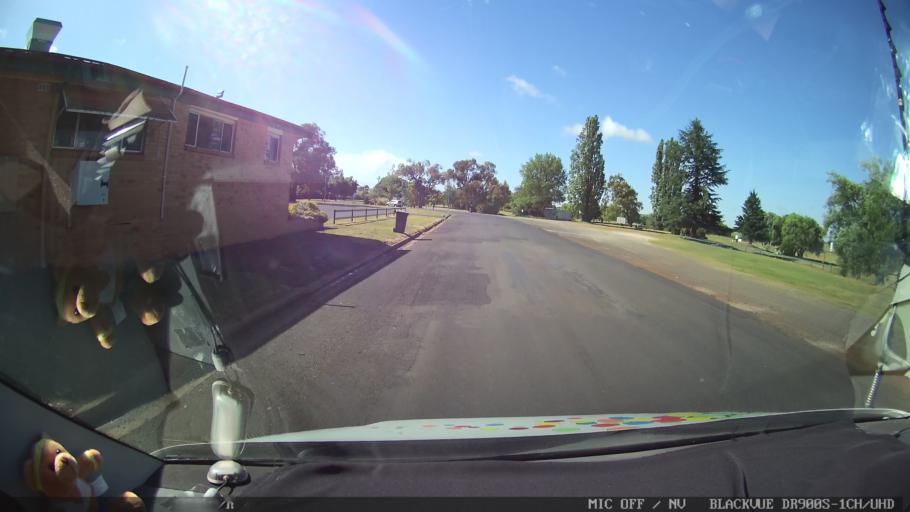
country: AU
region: New South Wales
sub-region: Guyra
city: Guyra
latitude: -30.2238
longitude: 151.6701
